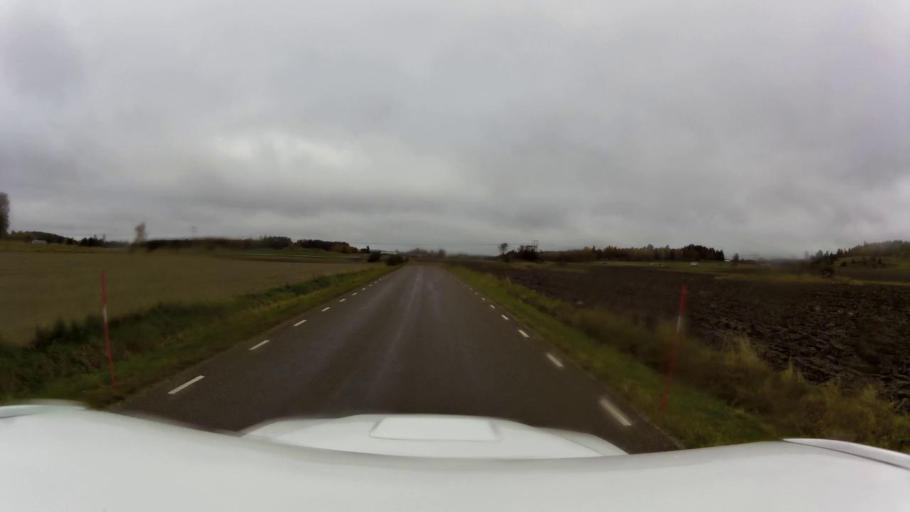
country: SE
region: OEstergoetland
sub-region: Linkopings Kommun
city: Linghem
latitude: 58.4695
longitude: 15.8227
